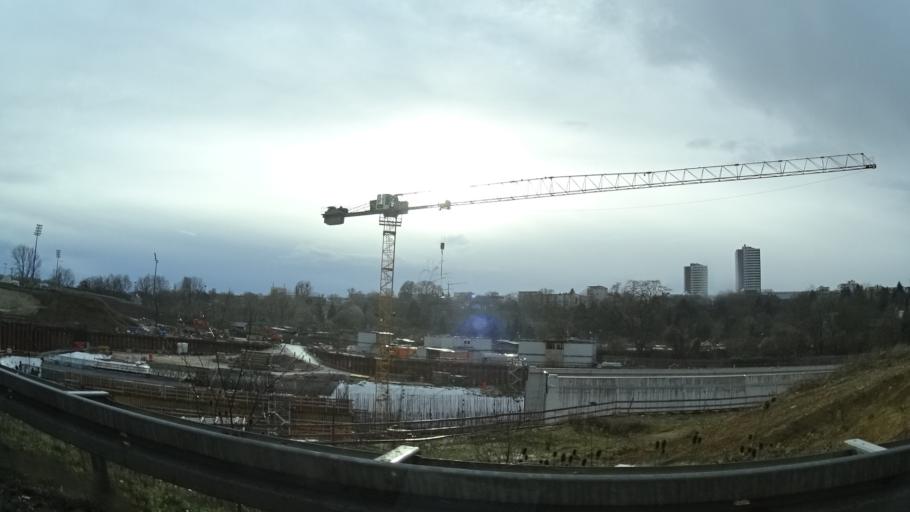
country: DE
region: Hesse
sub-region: Regierungsbezirk Darmstadt
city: Frankfurt am Main
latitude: 50.1318
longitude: 8.7248
